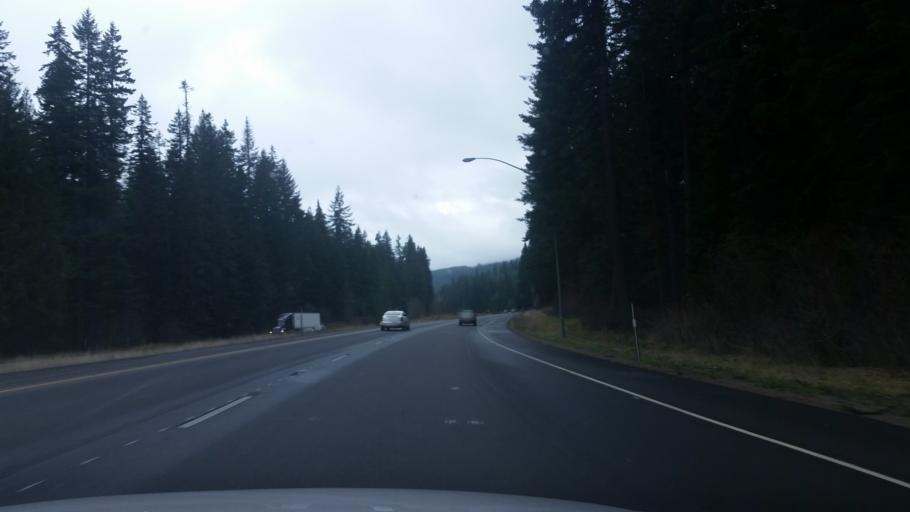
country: US
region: Washington
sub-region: Kittitas County
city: Cle Elum
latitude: 47.3096
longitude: -121.3120
